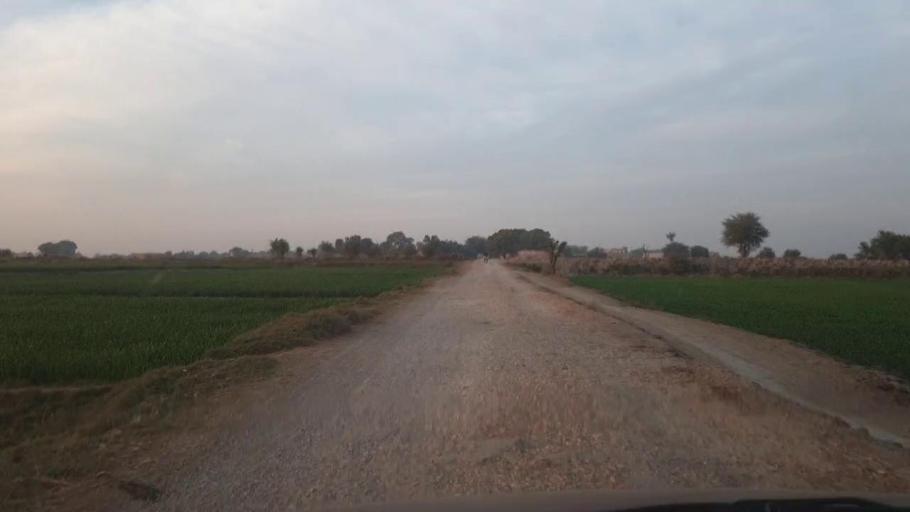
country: PK
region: Sindh
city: Shahpur Chakar
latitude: 26.0711
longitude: 68.5324
